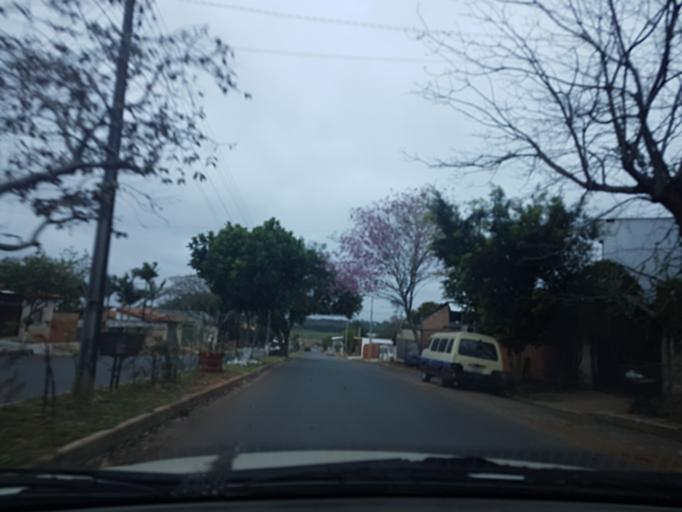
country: PY
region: Central
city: Colonia Mariano Roque Alonso
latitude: -25.2117
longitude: -57.5176
